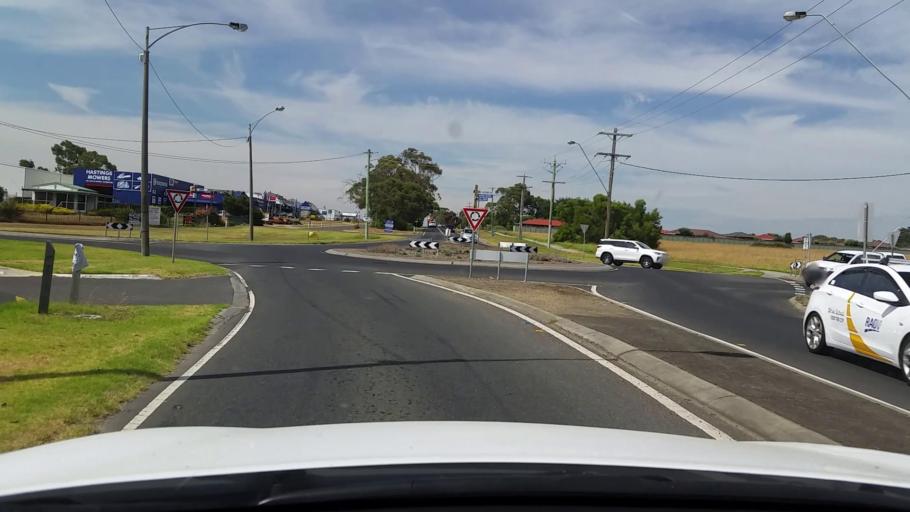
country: AU
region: Victoria
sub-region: Mornington Peninsula
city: Hastings
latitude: -38.2996
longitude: 145.1837
